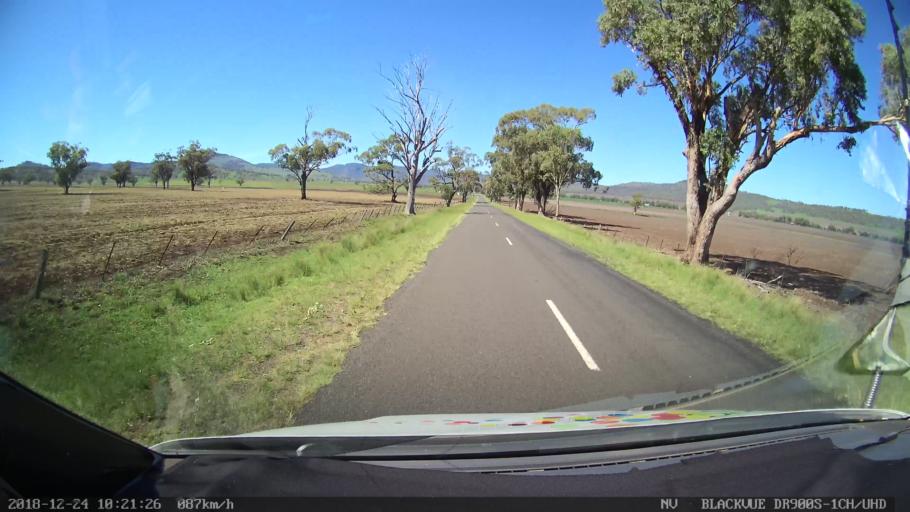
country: AU
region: New South Wales
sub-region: Liverpool Plains
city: Quirindi
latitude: -31.7522
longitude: 150.5508
